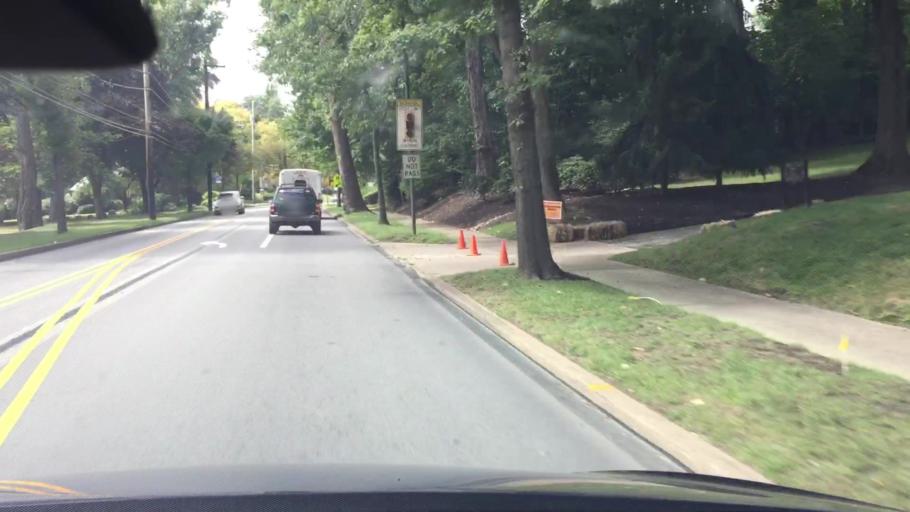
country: US
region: Pennsylvania
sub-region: Allegheny County
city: Oakmont
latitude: 40.5239
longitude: -79.8321
